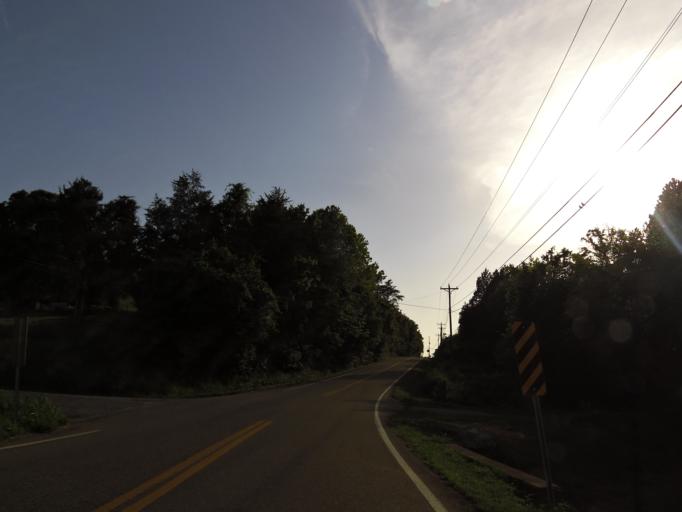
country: US
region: Tennessee
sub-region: Blount County
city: Louisville
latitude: 35.7821
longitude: -84.1143
